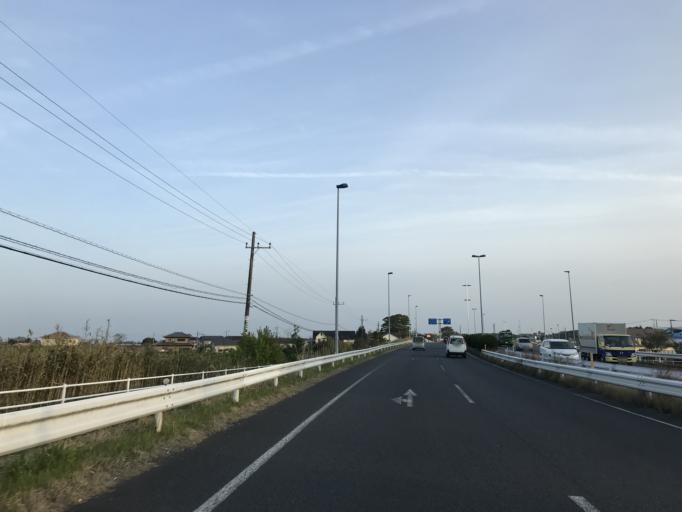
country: JP
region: Ibaraki
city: Katsuta
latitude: 36.3648
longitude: 140.5026
